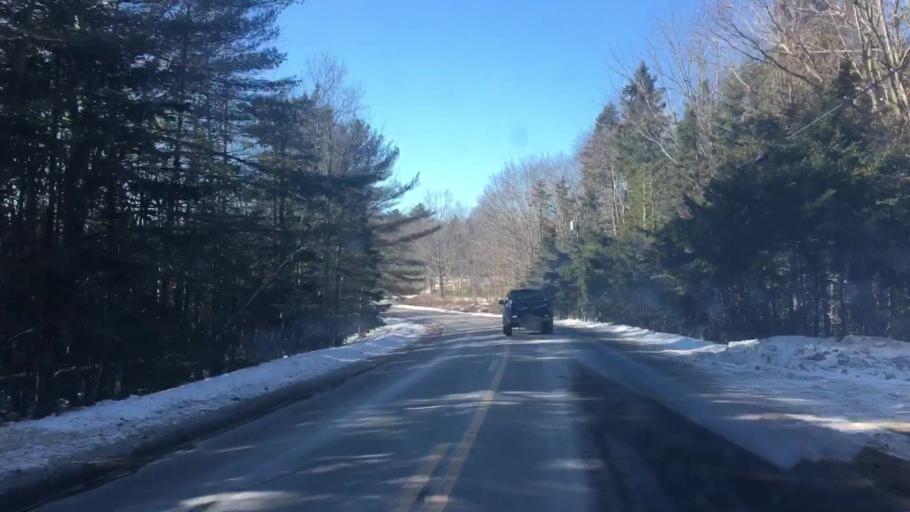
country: US
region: Maine
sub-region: Hancock County
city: Sedgwick
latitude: 44.3981
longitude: -68.6313
